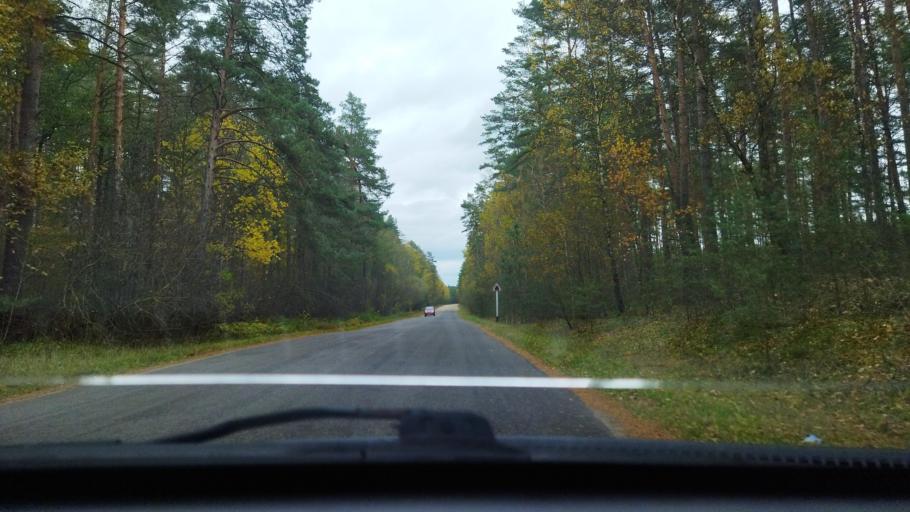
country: BY
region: Minsk
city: Svir
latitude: 54.8037
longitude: 26.2447
